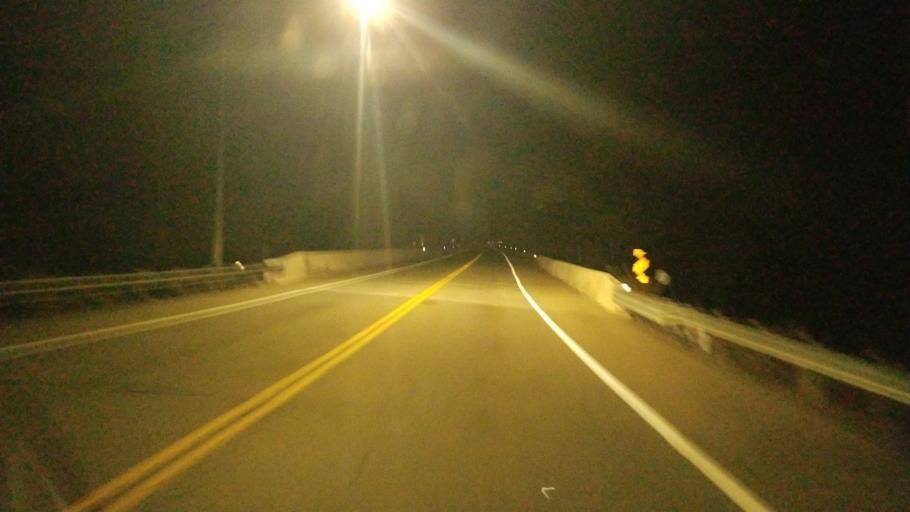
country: US
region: Ohio
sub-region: Stark County
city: Alliance
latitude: 40.9393
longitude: -81.1032
